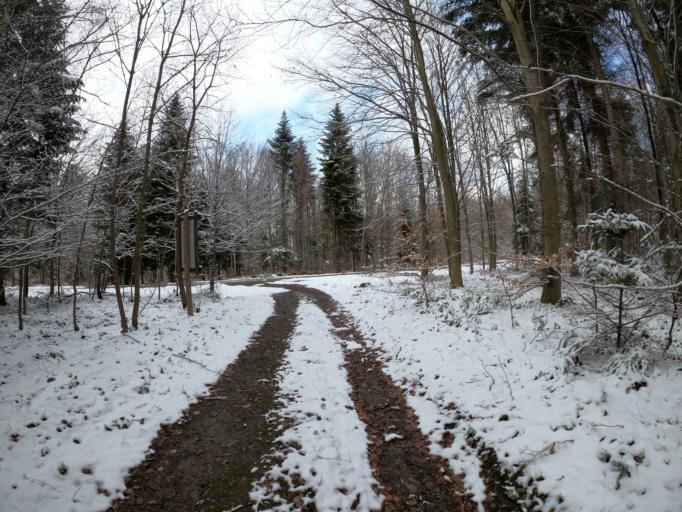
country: PL
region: Subcarpathian Voivodeship
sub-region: Powiat debicki
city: Debica
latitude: 49.9844
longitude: 21.4103
